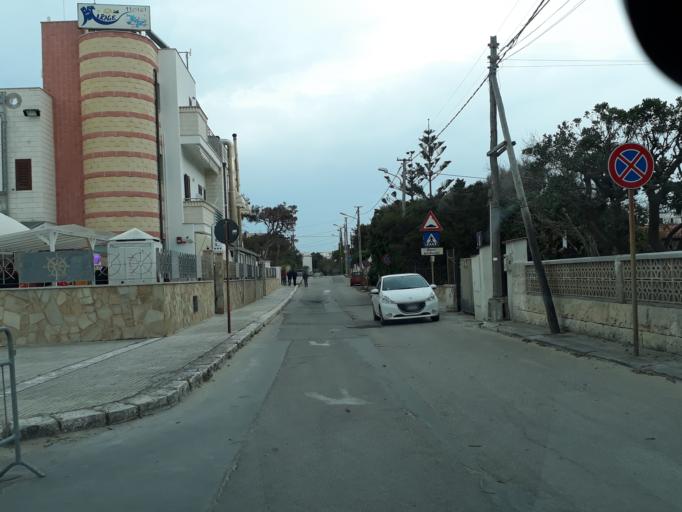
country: IT
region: Apulia
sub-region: Provincia di Brindisi
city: Carovigno
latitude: 40.7566
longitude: 17.7035
